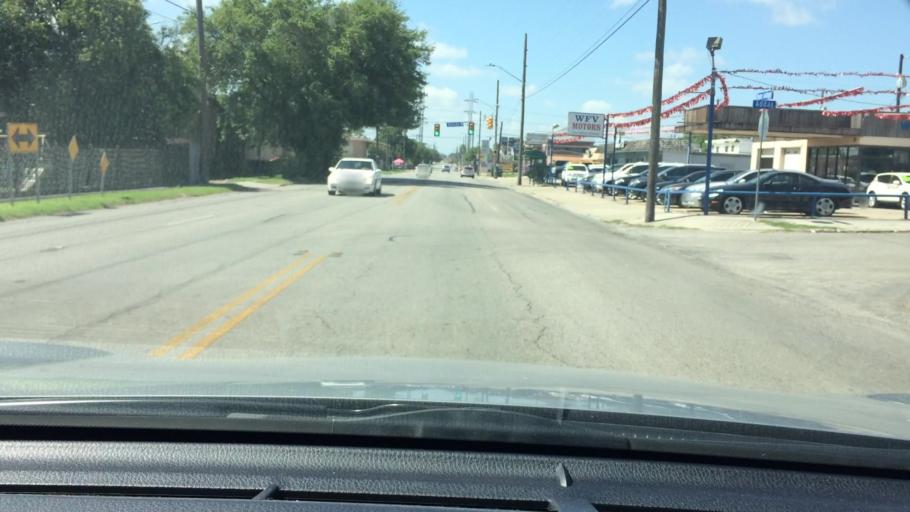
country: US
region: Texas
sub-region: Bexar County
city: Balcones Heights
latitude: 29.4958
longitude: -98.5351
